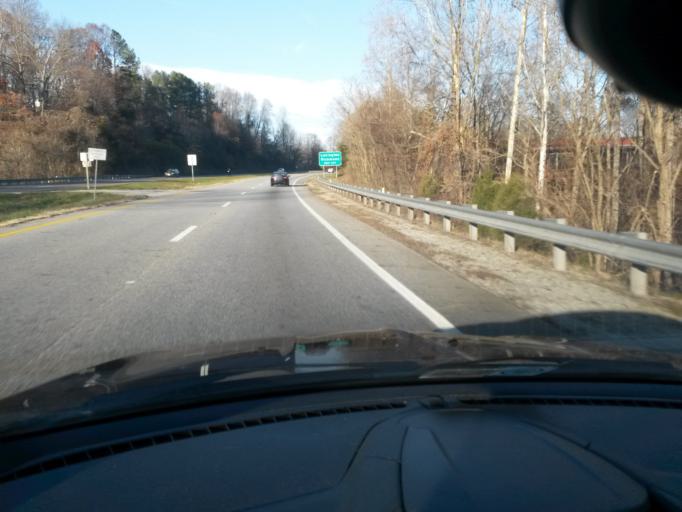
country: US
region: Virginia
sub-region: Amherst County
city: Amherst
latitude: 37.5760
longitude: -79.0512
